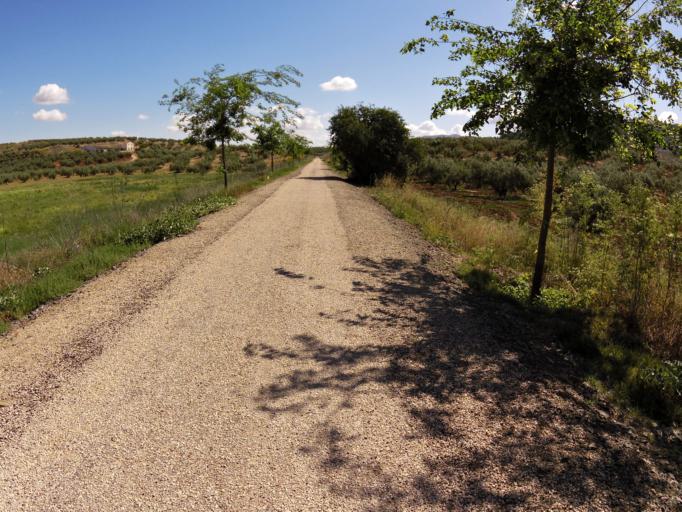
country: ES
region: Andalusia
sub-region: Provincia de Jaen
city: Alcaudete
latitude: 37.6018
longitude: -4.1370
